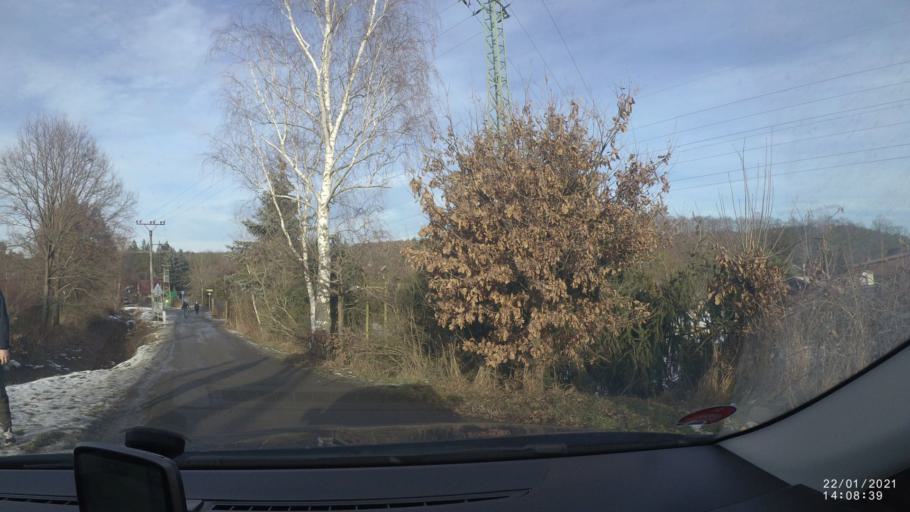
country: CZ
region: Plzensky
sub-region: Okres Plzen-Sever
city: Tremosna
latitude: 49.7856
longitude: 13.3861
